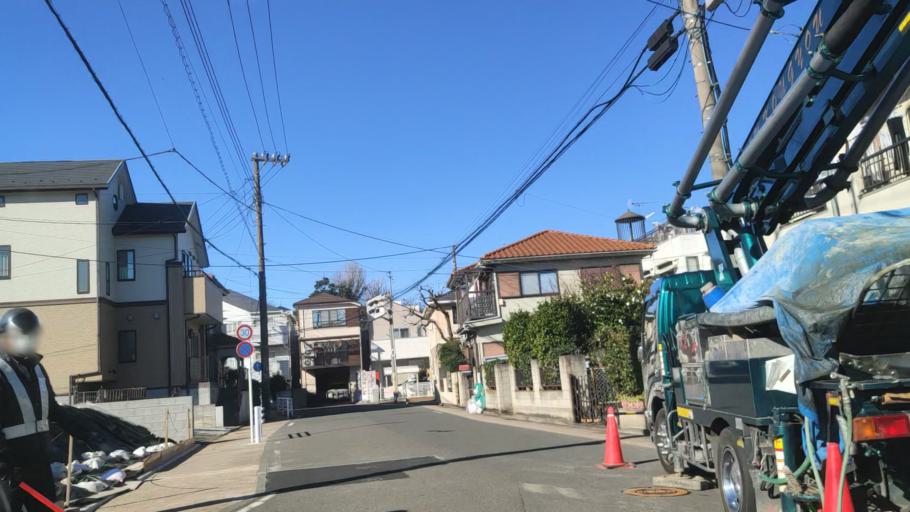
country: JP
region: Kanagawa
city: Yokohama
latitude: 35.4290
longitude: 139.6597
